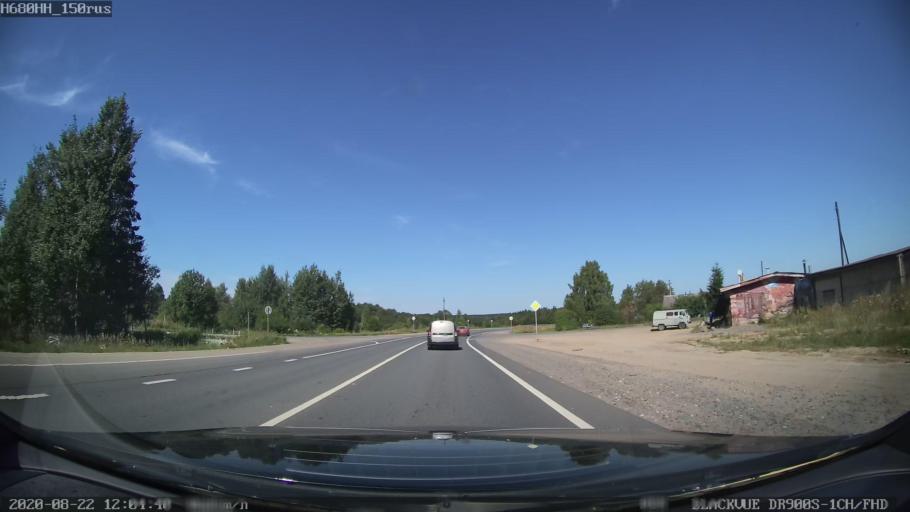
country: RU
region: Tverskaya
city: Rameshki
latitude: 57.2697
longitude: 36.0717
